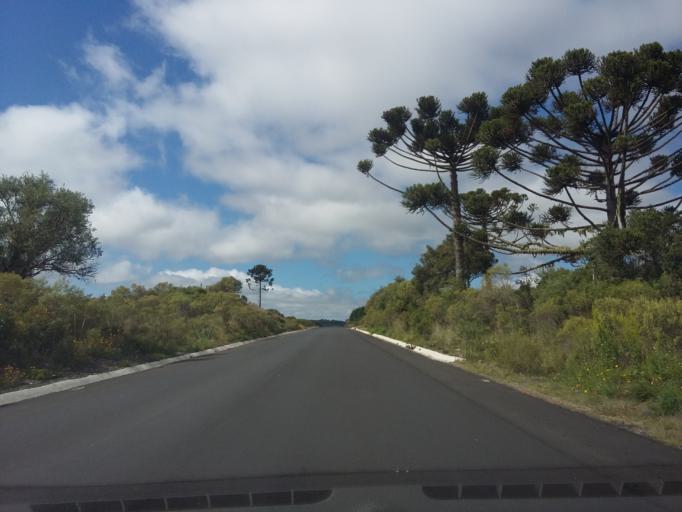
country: BR
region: Santa Catarina
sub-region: Sao Joaquim
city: Sao Joaquim
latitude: -28.0263
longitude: -50.0794
